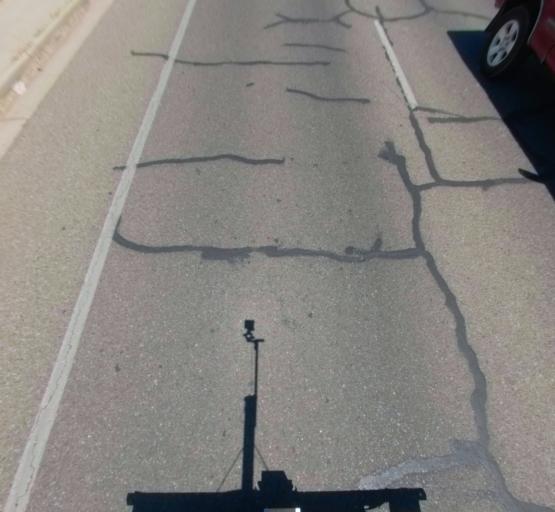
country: US
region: California
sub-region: Madera County
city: Madera
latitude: 36.9880
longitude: -120.0744
